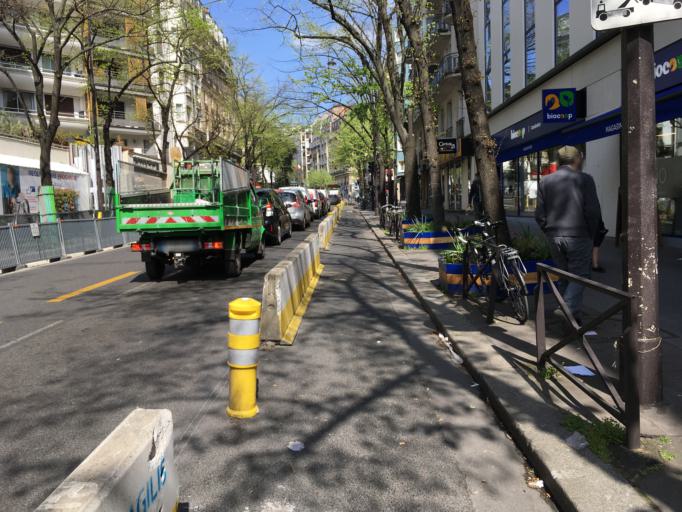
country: FR
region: Ile-de-France
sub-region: Departement de Seine-Saint-Denis
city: Bagnolet
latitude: 48.8706
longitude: 2.4035
